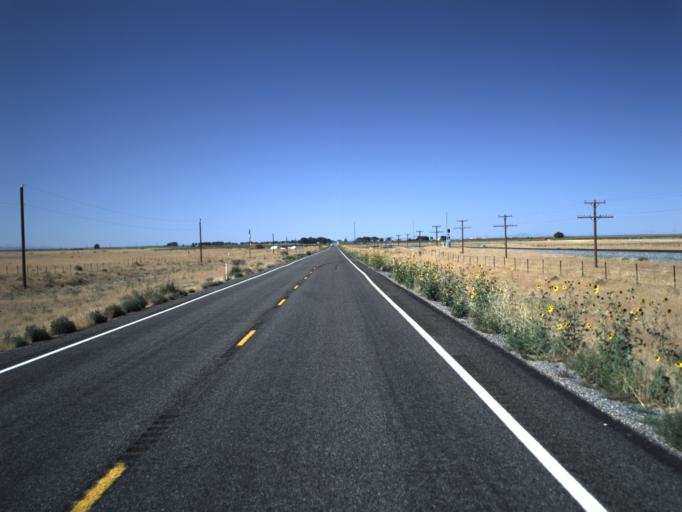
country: US
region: Utah
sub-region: Millard County
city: Delta
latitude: 39.5639
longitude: -112.3478
